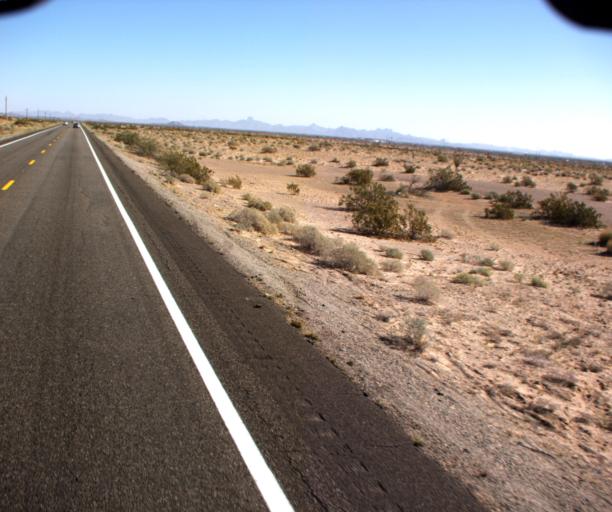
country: US
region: Arizona
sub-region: Yuma County
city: Fortuna Foothills
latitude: 32.8402
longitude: -114.3690
